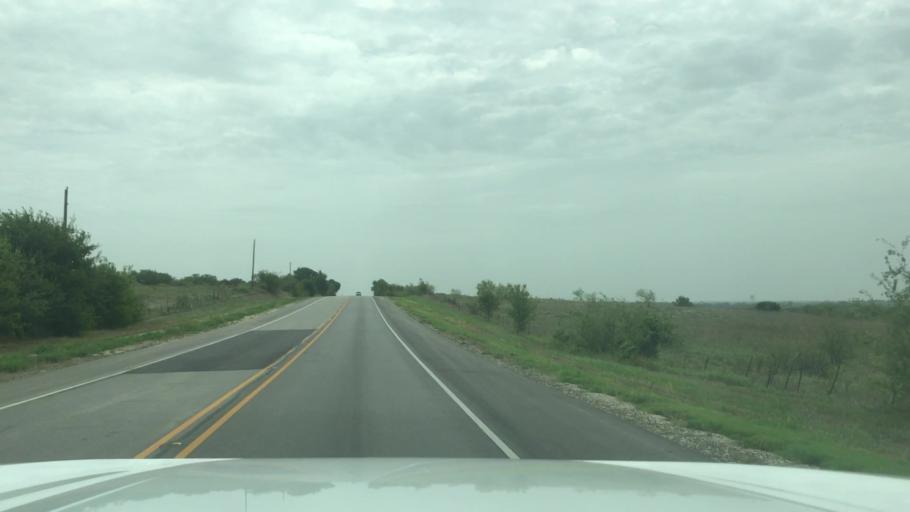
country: US
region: Texas
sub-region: Erath County
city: Dublin
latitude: 32.0816
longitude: -98.2461
